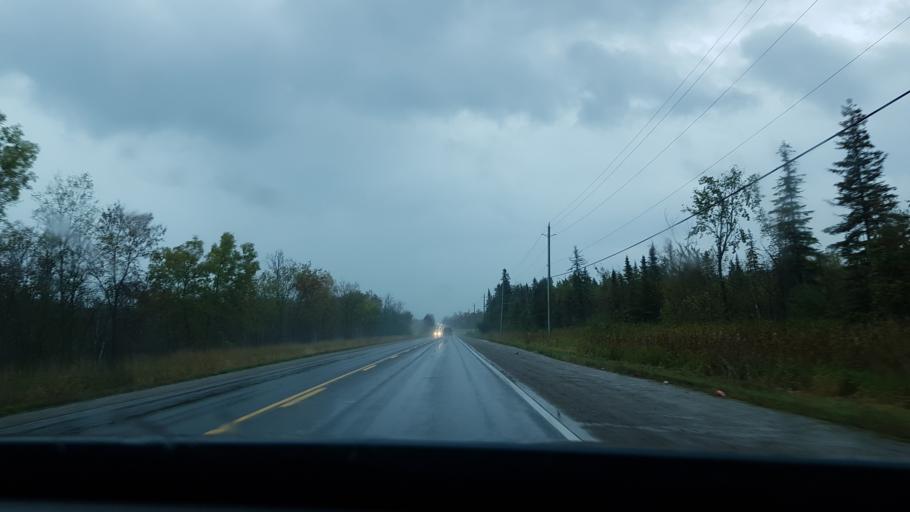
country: CA
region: Ontario
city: Peterborough
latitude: 44.3658
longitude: -78.3787
